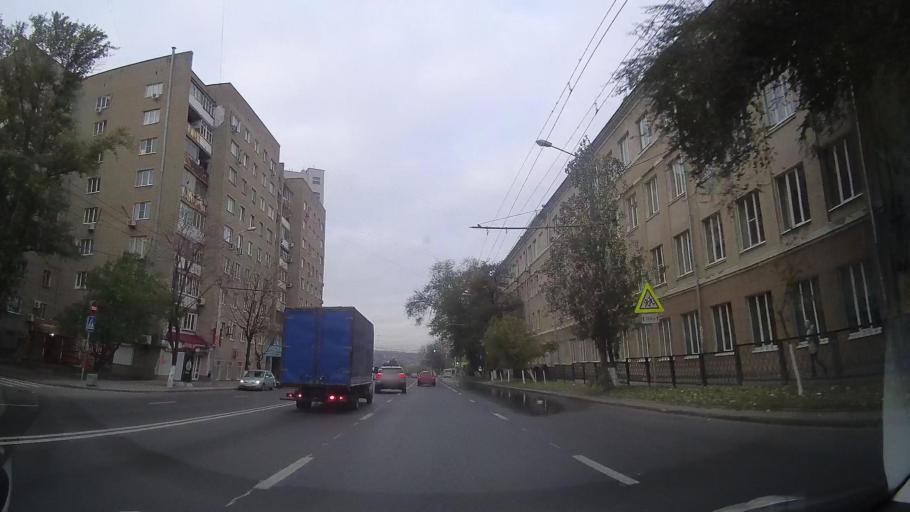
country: RU
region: Rostov
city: Rostov-na-Donu
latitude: 47.2248
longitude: 39.6977
